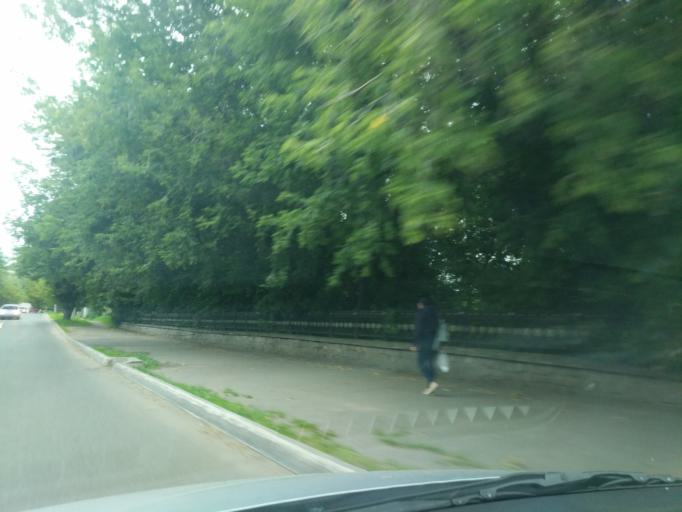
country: RU
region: Kirov
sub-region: Kirovo-Chepetskiy Rayon
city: Kirov
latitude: 58.5975
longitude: 49.6728
